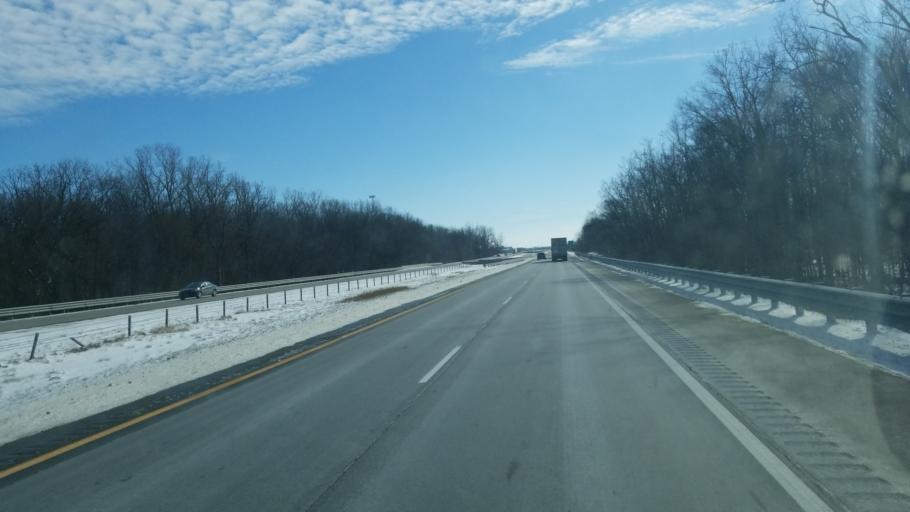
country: US
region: Michigan
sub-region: Monroe County
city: Dundee
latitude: 41.9849
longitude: -83.6787
